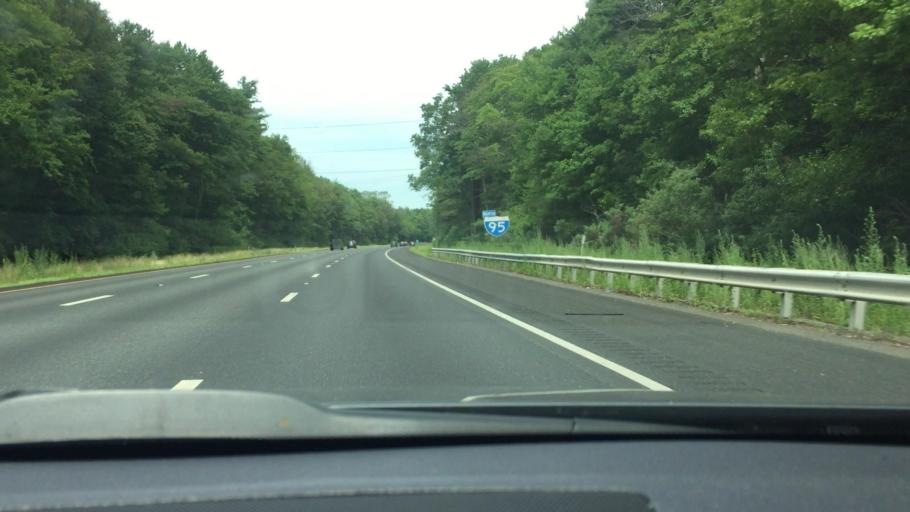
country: US
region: Massachusetts
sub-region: Norfolk County
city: Walpole
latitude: 42.1074
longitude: -71.2303
